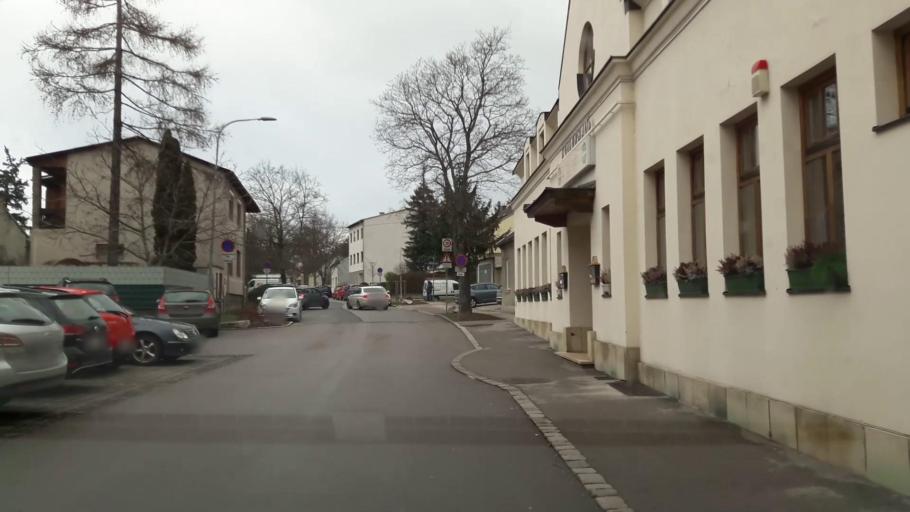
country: AT
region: Lower Austria
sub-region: Politischer Bezirk Wien-Umgebung
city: Himberg
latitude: 48.1003
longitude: 16.4228
